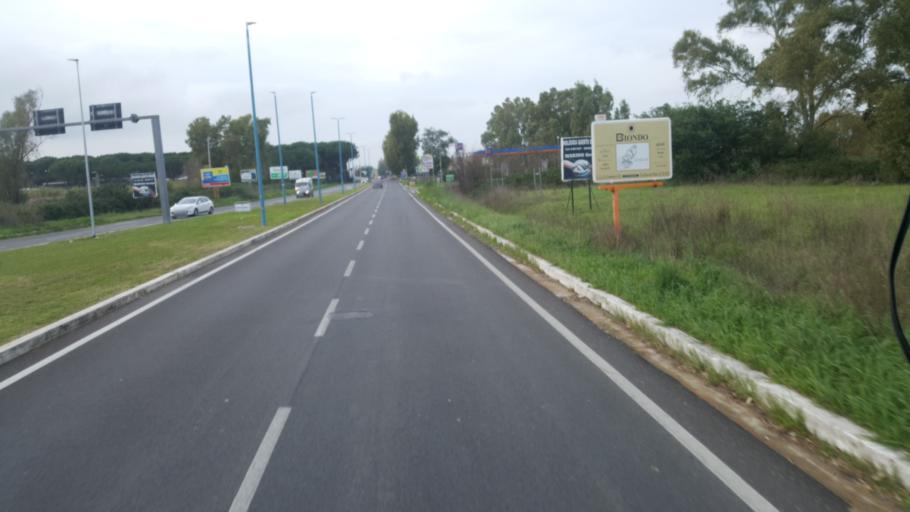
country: IT
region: Latium
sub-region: Provincia di Latina
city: Latina
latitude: 41.4784
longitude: 12.8736
